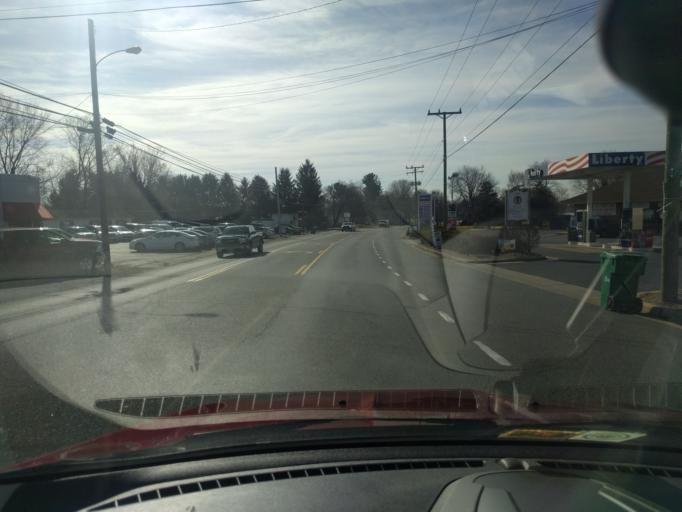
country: US
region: Virginia
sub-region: Rockingham County
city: Bridgewater
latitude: 38.3625
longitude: -78.9377
